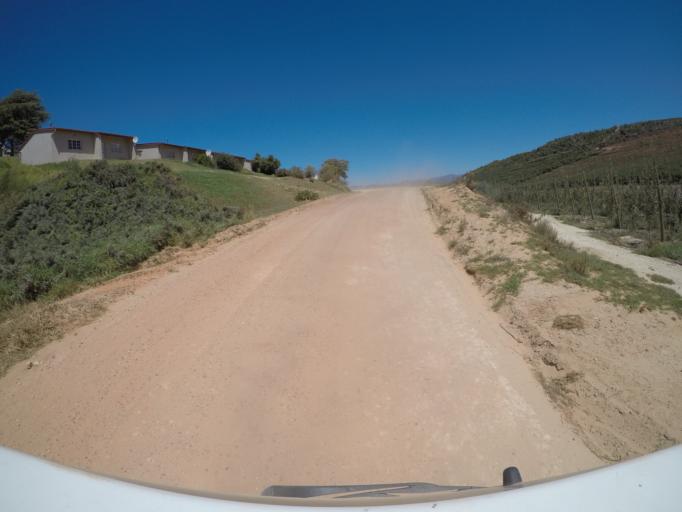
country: ZA
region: Western Cape
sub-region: Overberg District Municipality
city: Grabouw
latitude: -34.2441
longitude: 19.1084
